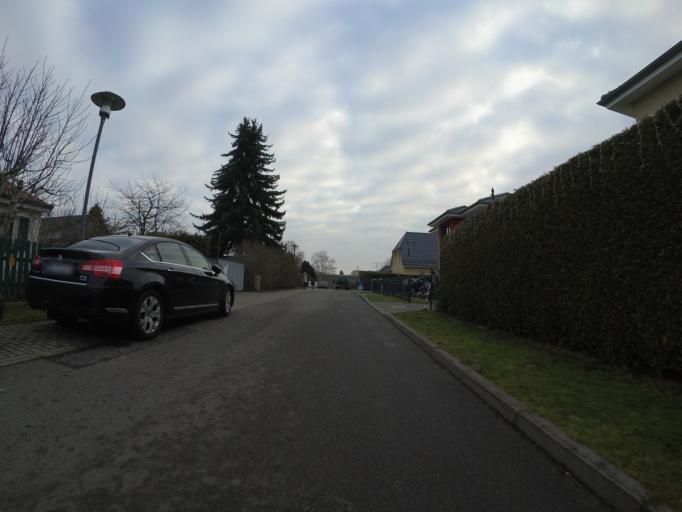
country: DE
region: Brandenburg
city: Ahrensfelde
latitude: 52.5662
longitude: 13.5874
